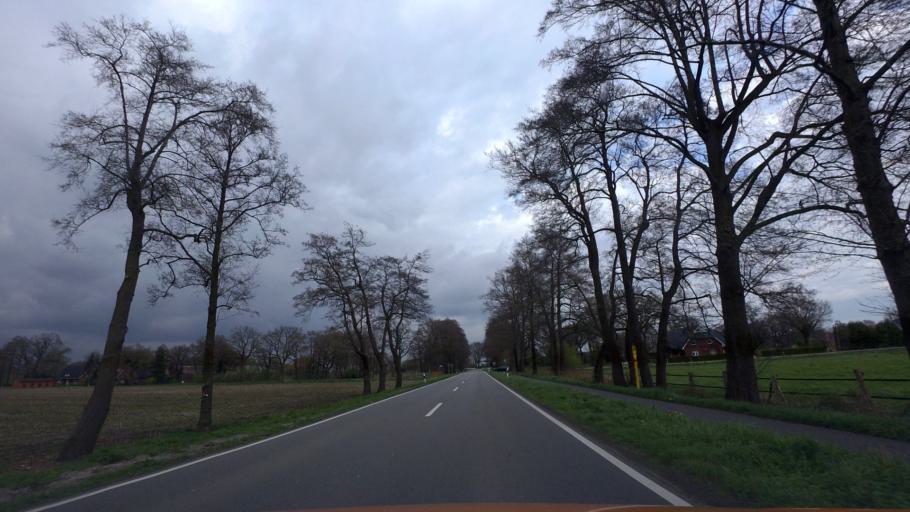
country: DE
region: Lower Saxony
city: Friesoythe
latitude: 53.0391
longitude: 7.8880
